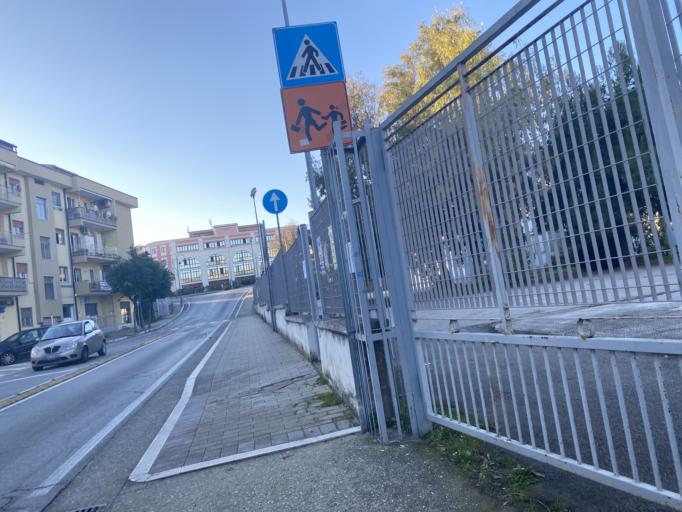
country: IT
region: Campania
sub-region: Provincia di Salerno
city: Agropoli
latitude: 40.3496
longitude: 14.9937
